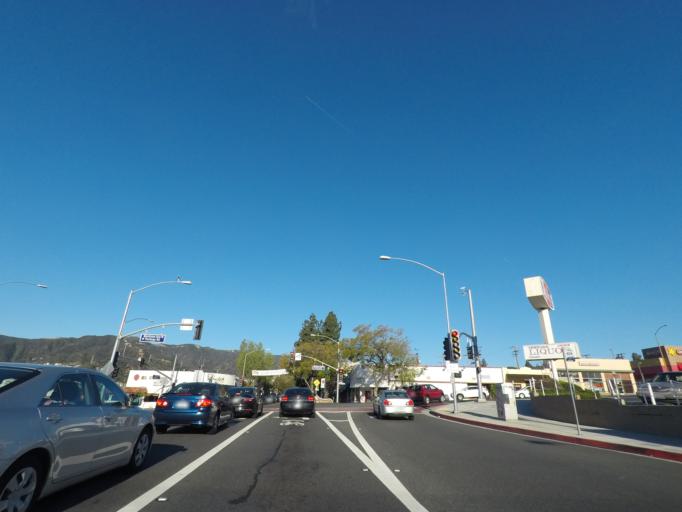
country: US
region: California
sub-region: Los Angeles County
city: La Crescenta-Montrose
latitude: 34.2050
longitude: -118.2247
